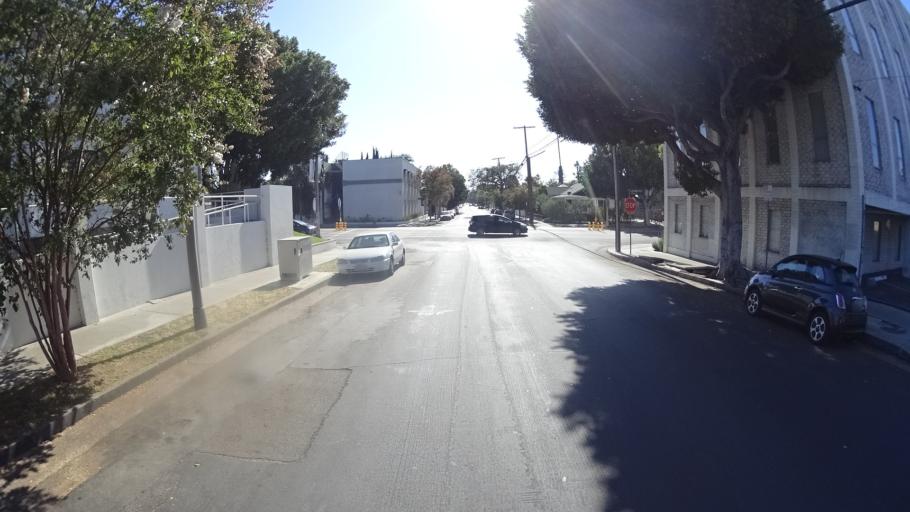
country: US
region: California
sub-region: Los Angeles County
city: Hollywood
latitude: 34.0817
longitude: -118.3233
